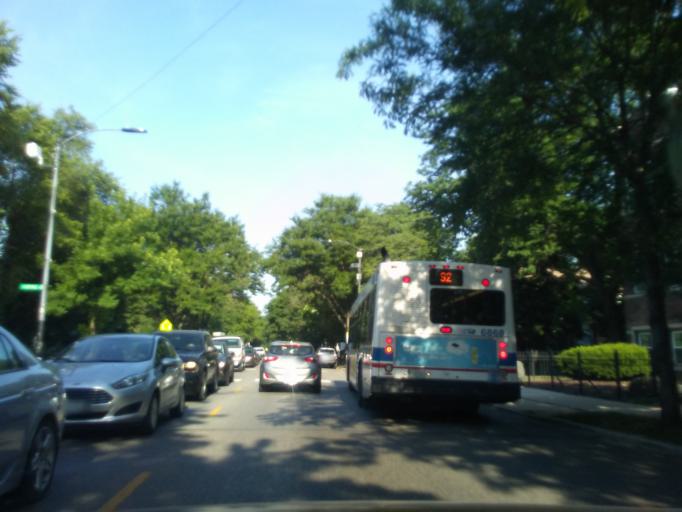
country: US
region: Illinois
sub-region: Cook County
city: Lincolnwood
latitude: 41.9761
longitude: -87.6815
